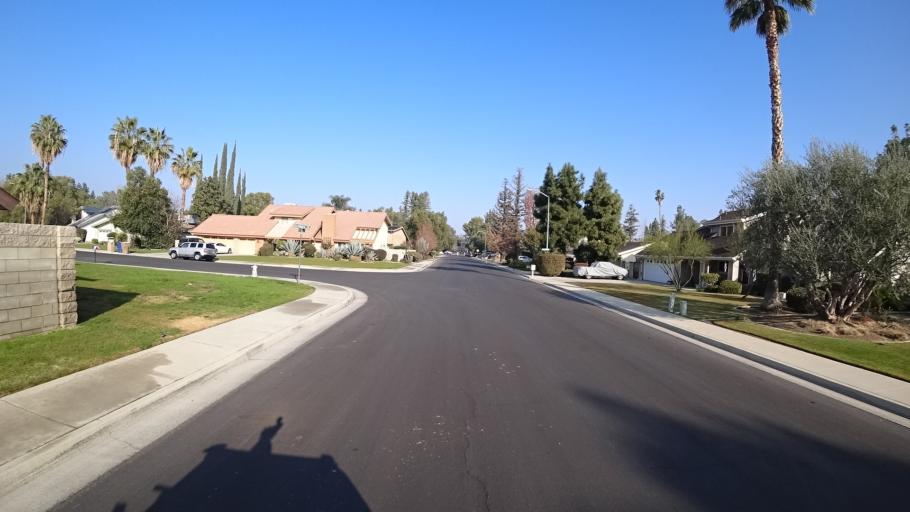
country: US
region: California
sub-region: Kern County
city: Greenacres
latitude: 35.3417
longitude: -119.0716
